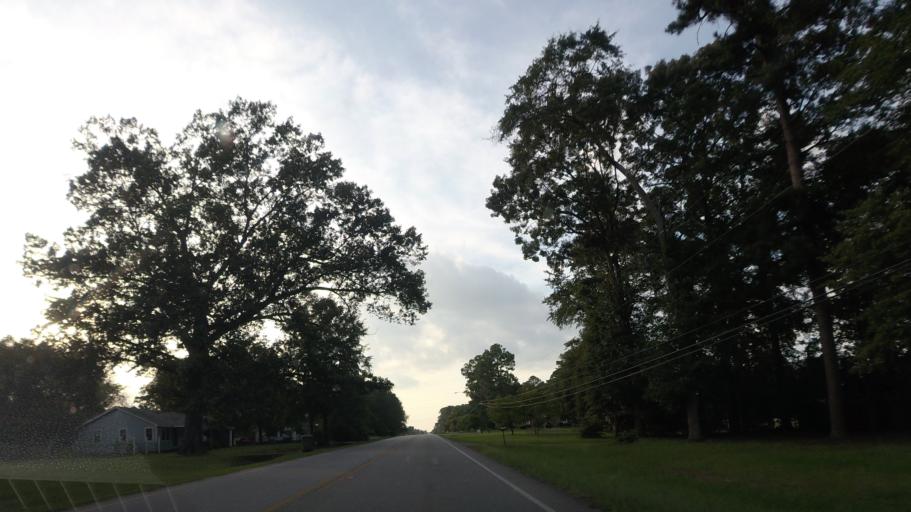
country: US
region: Georgia
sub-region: Wilkinson County
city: Gordon
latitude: 32.8869
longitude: -83.3481
